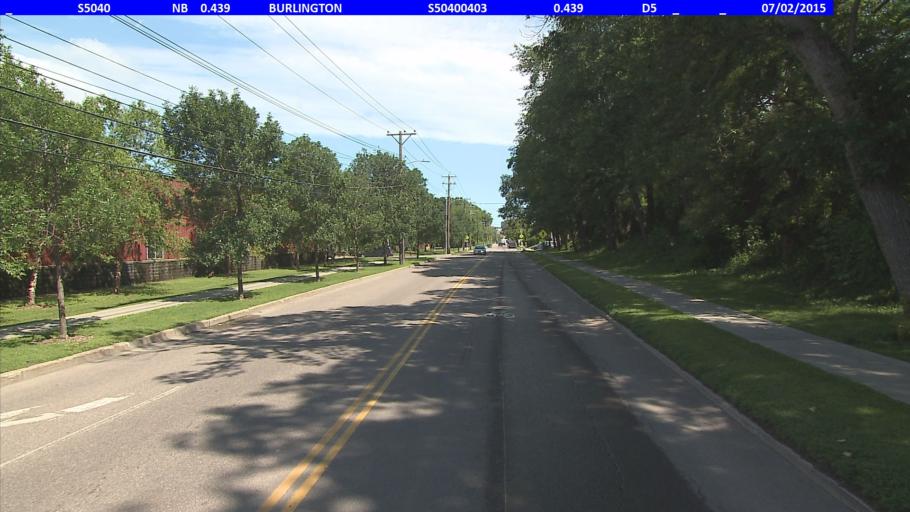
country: US
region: Vermont
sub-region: Chittenden County
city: Burlington
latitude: 44.4618
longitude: -73.2146
